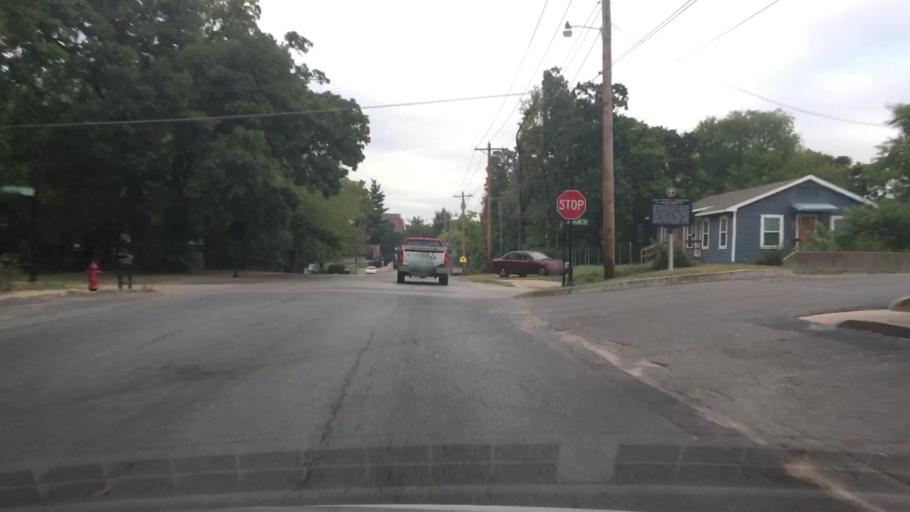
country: US
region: Oklahoma
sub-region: Cherokee County
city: Tahlequah
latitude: 35.9157
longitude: -94.9714
